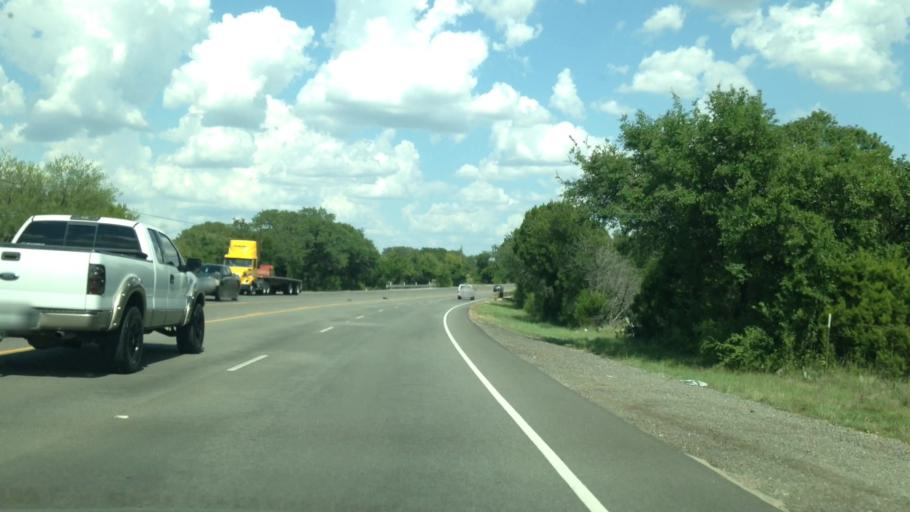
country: US
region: Texas
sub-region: Williamson County
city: Georgetown
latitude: 30.6342
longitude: -97.7289
